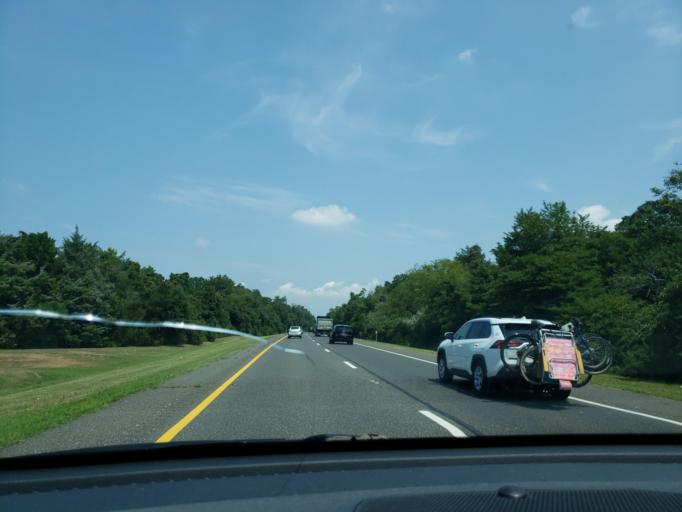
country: US
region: New Jersey
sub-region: Cape May County
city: Erma
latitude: 38.9721
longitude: -74.8952
